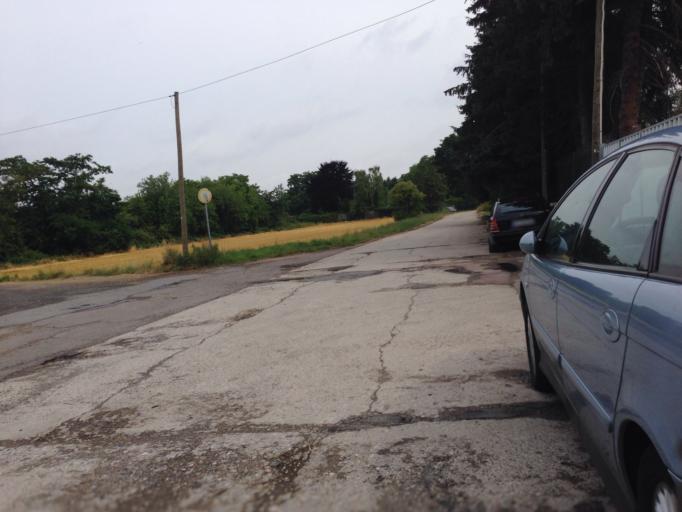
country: DE
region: Hesse
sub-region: Regierungsbezirk Darmstadt
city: Grosskrotzenburg
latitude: 50.0959
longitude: 8.9456
